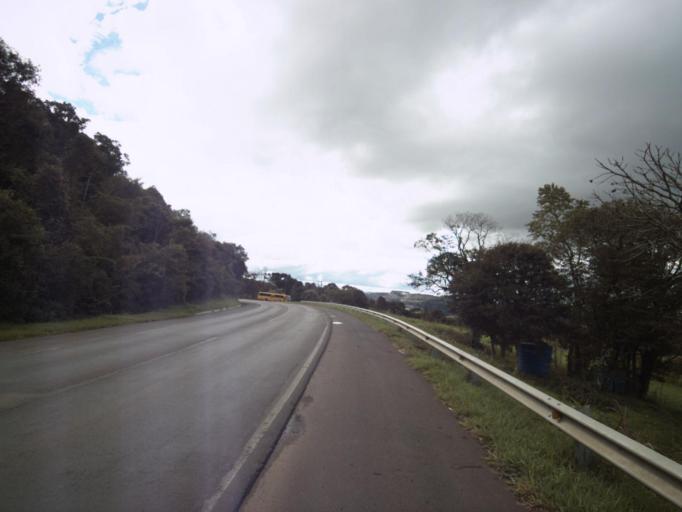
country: BR
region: Santa Catarina
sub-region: Concordia
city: Concordia
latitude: -27.2613
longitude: -51.9542
